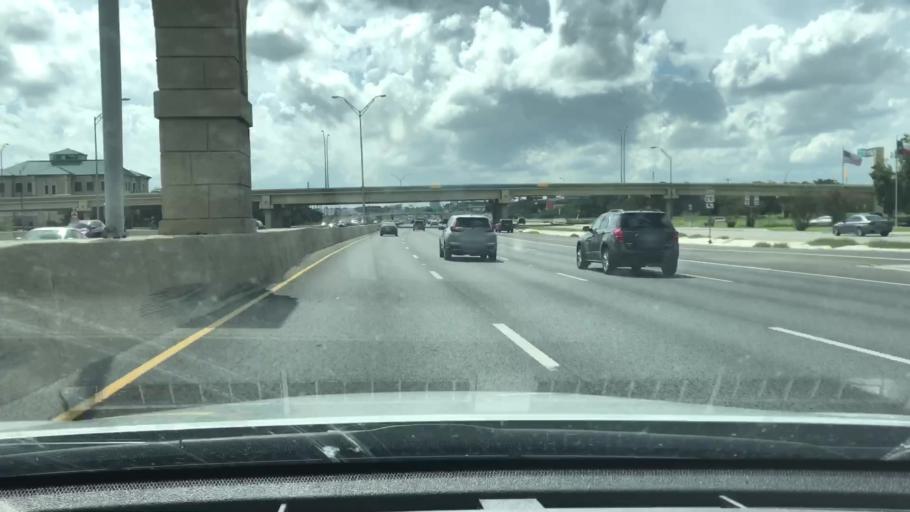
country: US
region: Texas
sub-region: Bexar County
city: Hollywood Park
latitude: 29.5560
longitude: -98.4854
